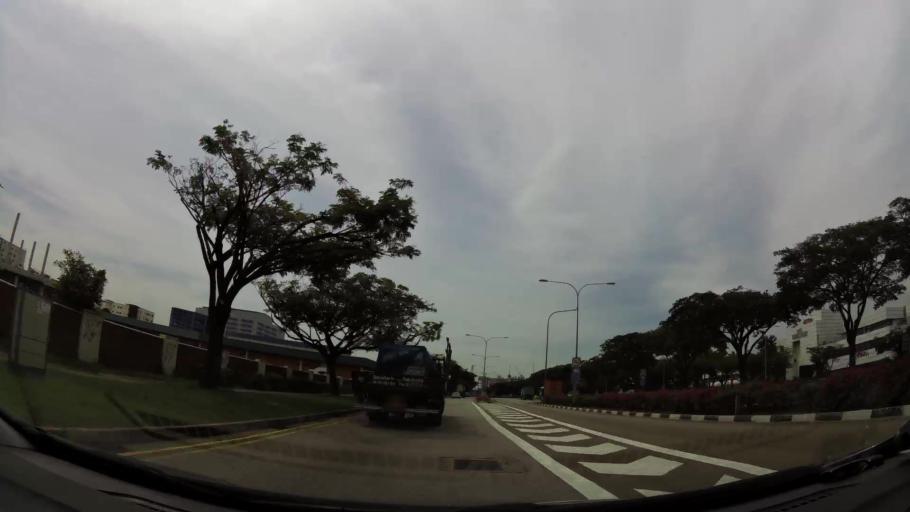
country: MY
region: Johor
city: Johor Bahru
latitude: 1.3223
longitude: 103.6760
